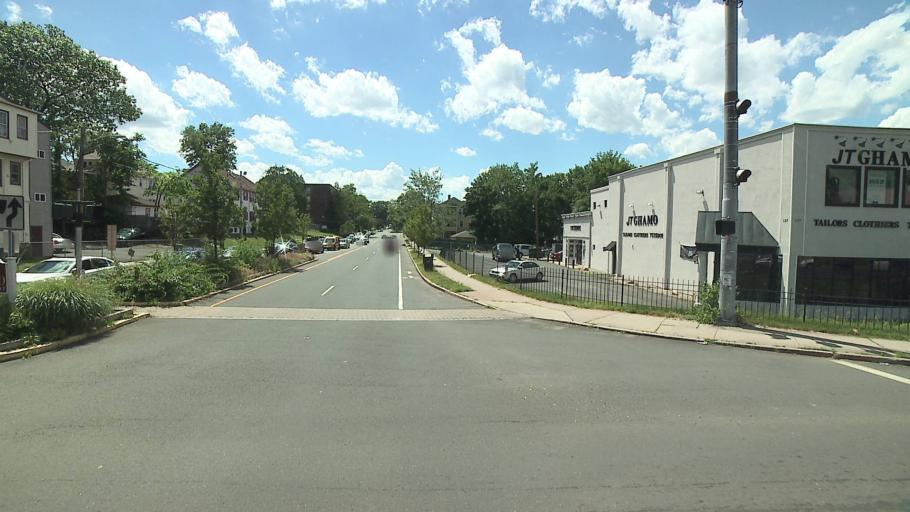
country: US
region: Connecticut
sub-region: Hartford County
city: Hartford
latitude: 41.7618
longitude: -72.7067
